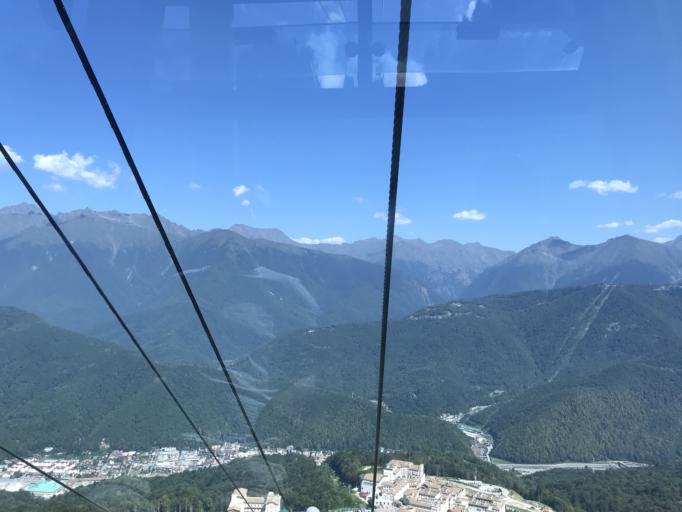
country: RU
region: Krasnodarskiy
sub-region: Sochi City
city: Krasnaya Polyana
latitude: 43.6623
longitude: 40.2536
